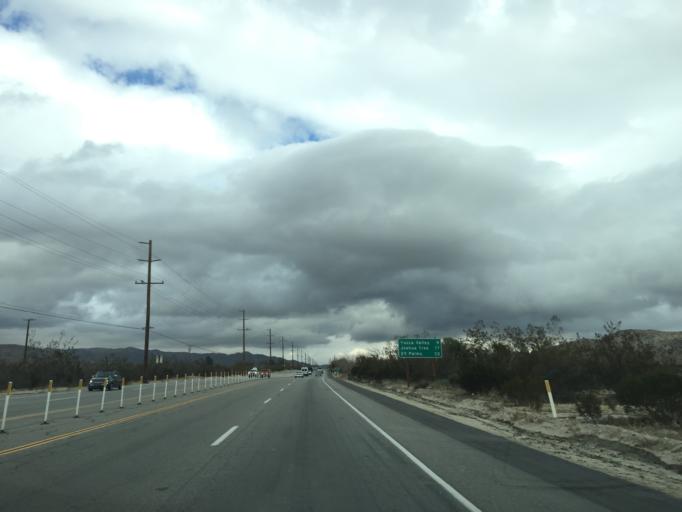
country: US
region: California
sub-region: San Bernardino County
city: Morongo Valley
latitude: 34.0566
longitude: -116.5699
